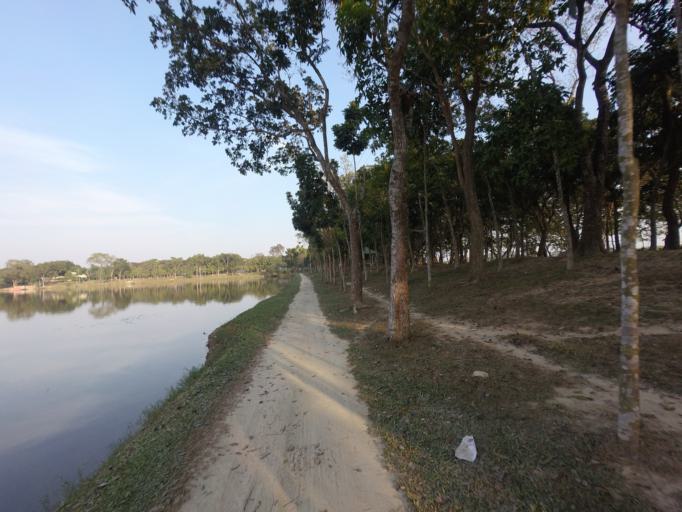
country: BD
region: Rajshahi
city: Saidpur
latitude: 26.0013
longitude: 88.7552
